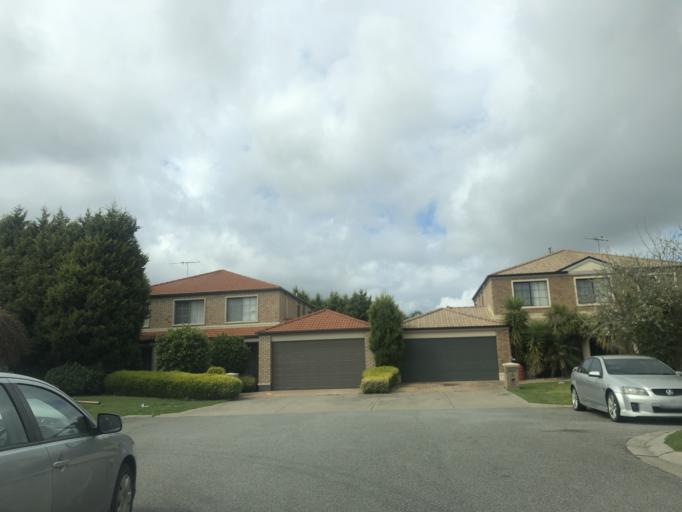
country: AU
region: Victoria
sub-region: Knox
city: Rowville
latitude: -37.9405
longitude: 145.2262
